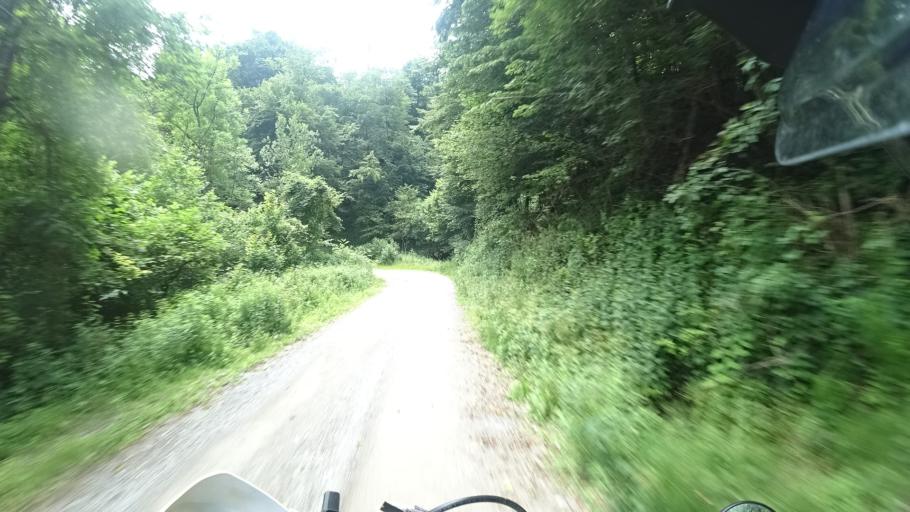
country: SI
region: Osilnica
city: Osilnica
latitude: 45.5244
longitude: 14.7299
